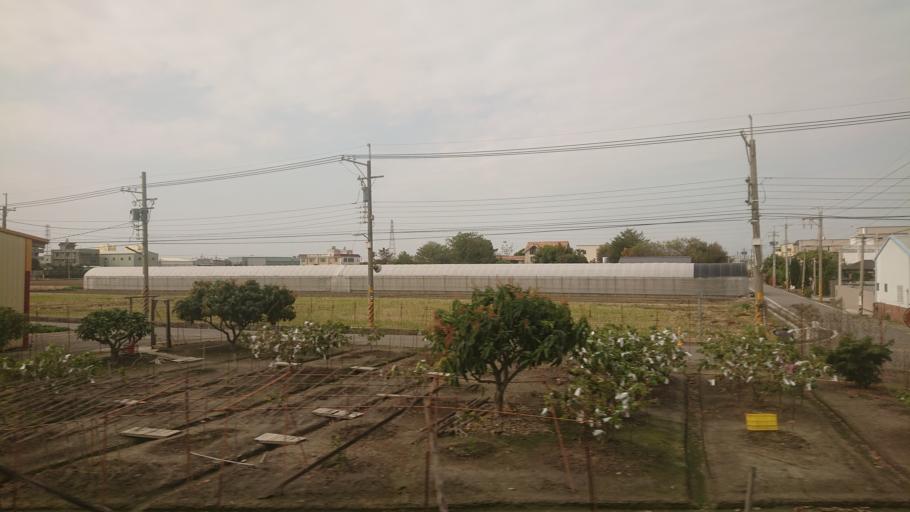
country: TW
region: Taiwan
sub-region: Changhua
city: Chang-hua
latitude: 24.0329
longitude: 120.5336
